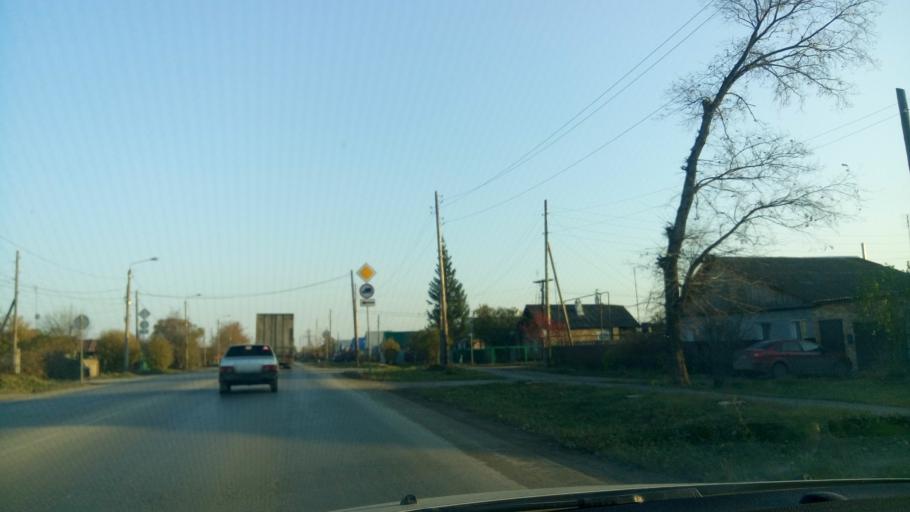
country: RU
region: Sverdlovsk
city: Bogdanovich
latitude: 56.7647
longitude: 62.0663
